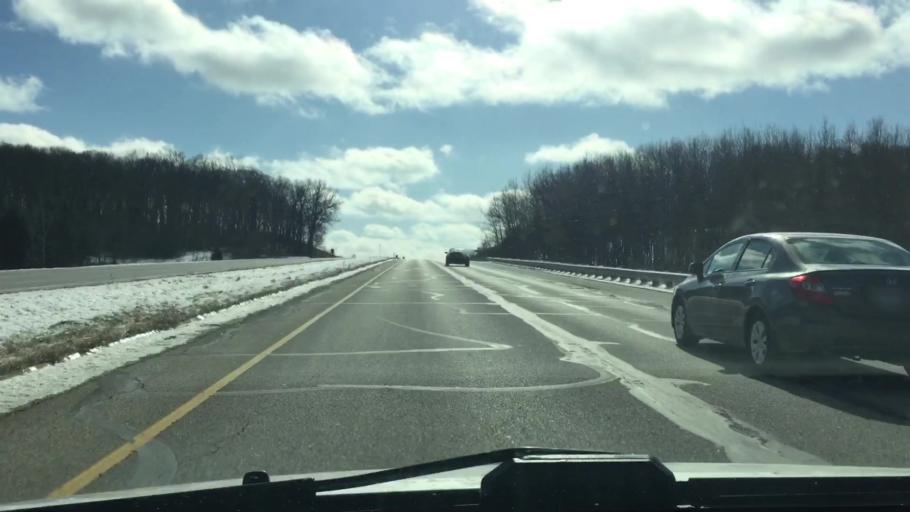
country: US
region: Wisconsin
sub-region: Waukesha County
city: Big Bend
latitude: 42.9395
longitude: -88.2284
